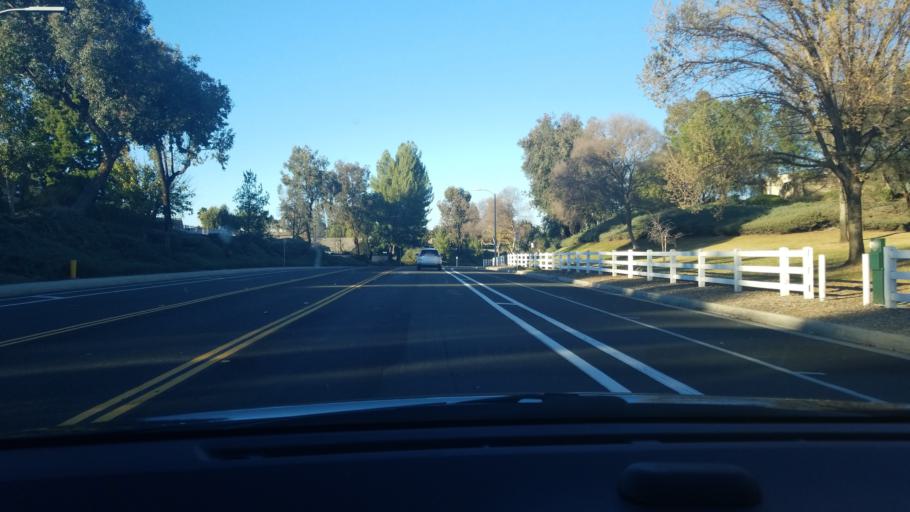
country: US
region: California
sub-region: Riverside County
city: Temecula
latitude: 33.5178
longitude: -117.1217
